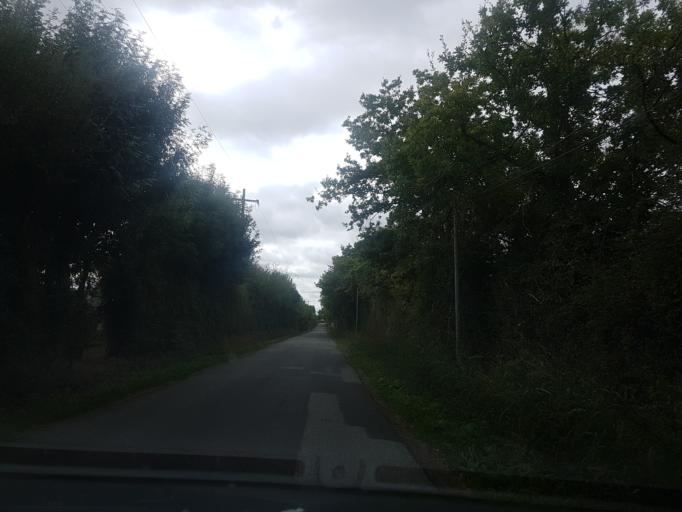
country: FR
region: Pays de la Loire
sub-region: Departement de la Loire-Atlantique
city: Ligne
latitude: 47.4092
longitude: -1.3828
